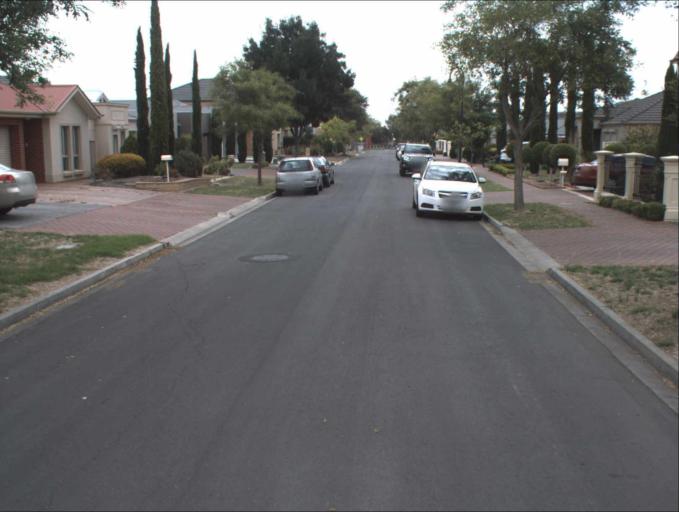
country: AU
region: South Australia
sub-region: Port Adelaide Enfield
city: Gilles Plains
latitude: -34.8534
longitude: 138.6355
